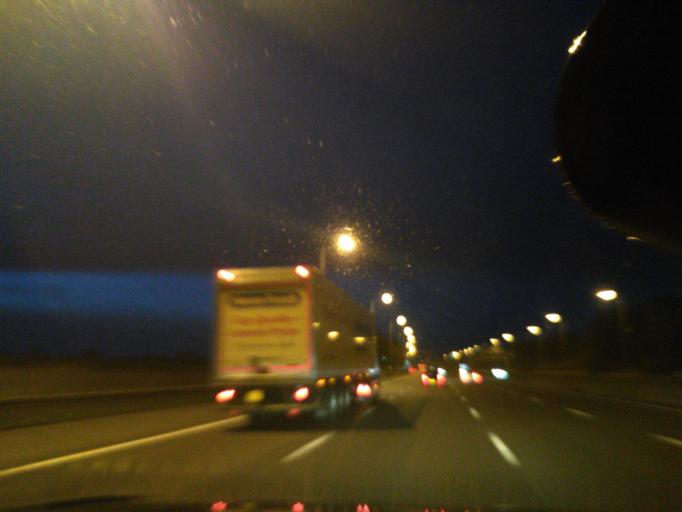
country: GB
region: England
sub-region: Derbyshire
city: Pinxton
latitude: 53.0857
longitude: -1.3005
